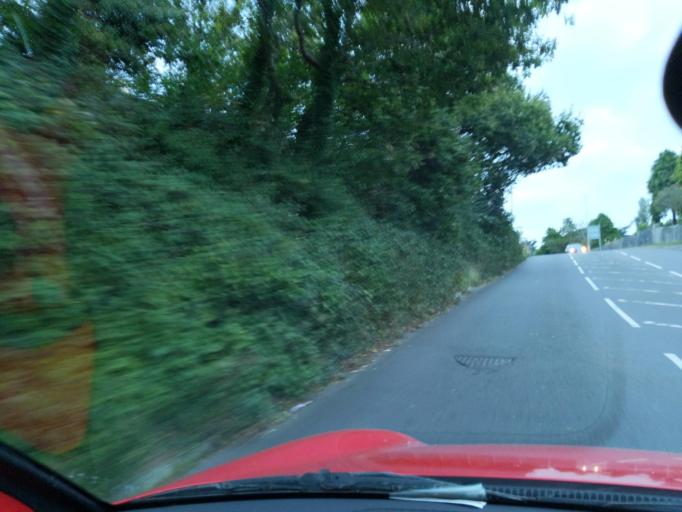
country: GB
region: England
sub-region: Cornwall
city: Torpoint
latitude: 50.4003
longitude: -4.1706
